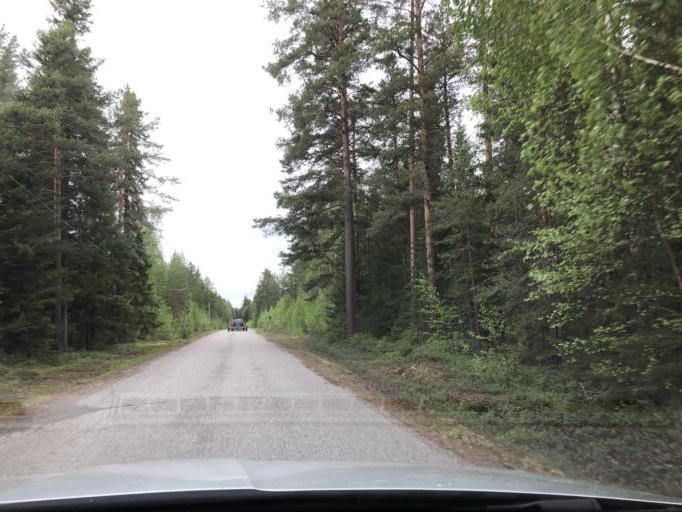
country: SE
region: Norrbotten
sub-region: Pitea Kommun
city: Roknas
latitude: 65.3806
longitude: 21.2737
